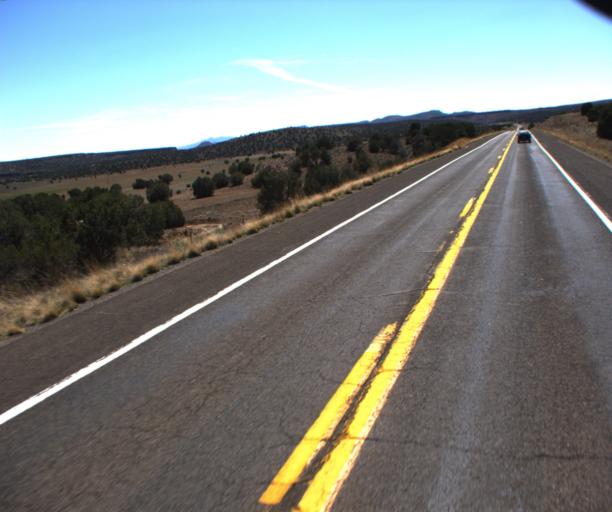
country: US
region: Arizona
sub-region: Mohave County
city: Peach Springs
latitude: 35.4597
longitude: -113.6153
